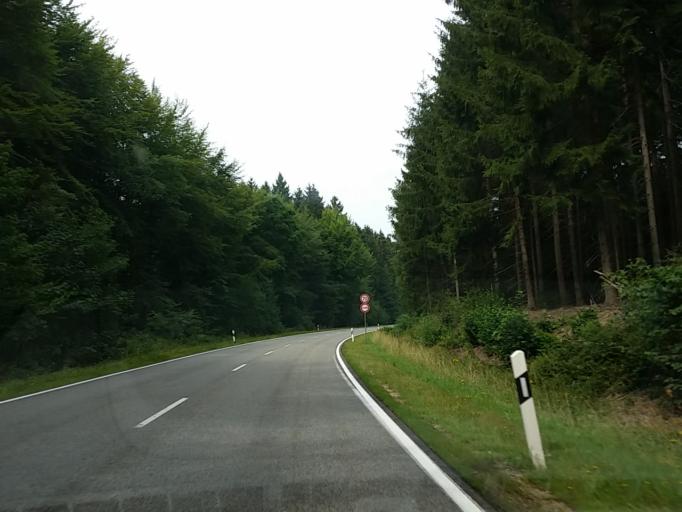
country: DE
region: Rheinland-Pfalz
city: Farschweiler
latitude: 49.7096
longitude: 6.8265
